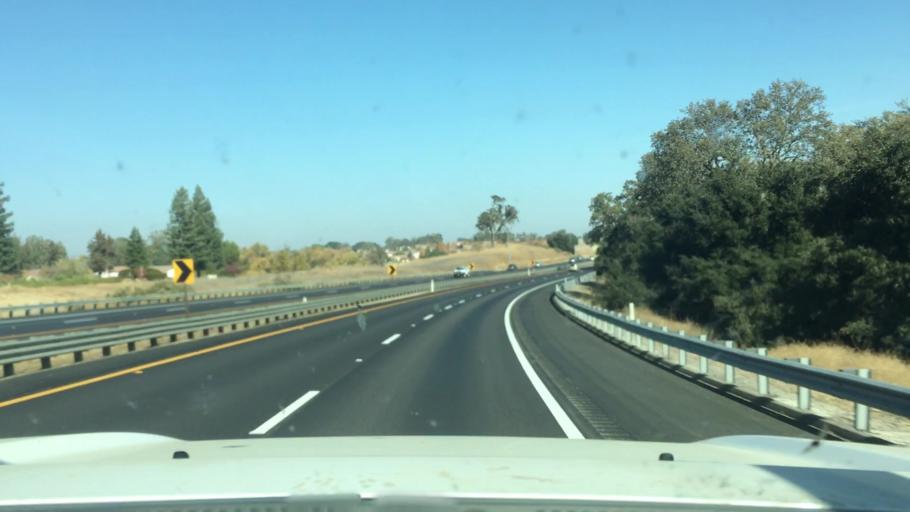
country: US
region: California
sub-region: San Luis Obispo County
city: Templeton
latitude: 35.5672
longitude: -120.7084
